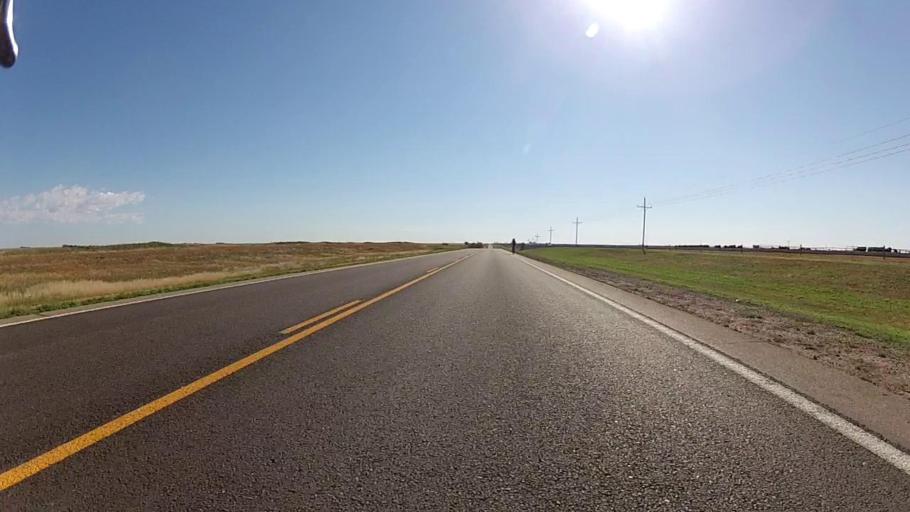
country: US
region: Kansas
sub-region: Haskell County
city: Sublette
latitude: 37.5632
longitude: -100.5609
